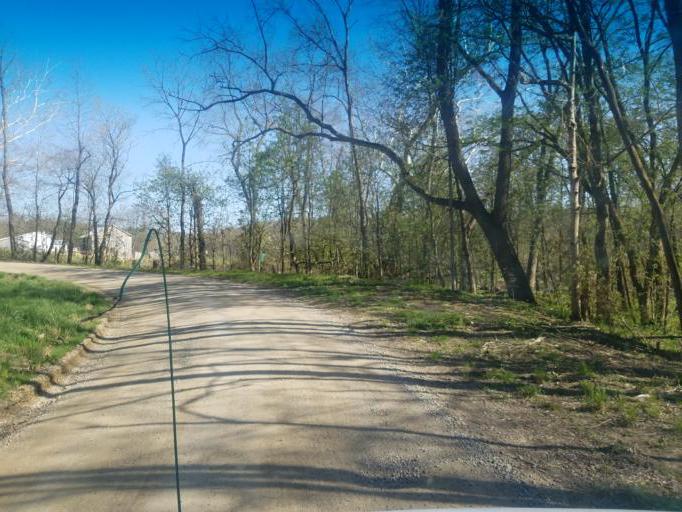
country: US
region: Ohio
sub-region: Muskingum County
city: Frazeysburg
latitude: 40.2179
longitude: -82.1804
